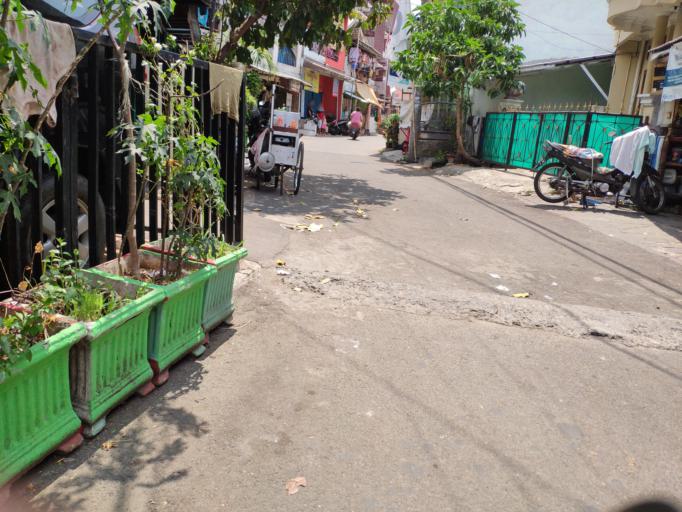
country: ID
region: Jakarta Raya
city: Jakarta
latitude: -6.2127
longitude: 106.8709
